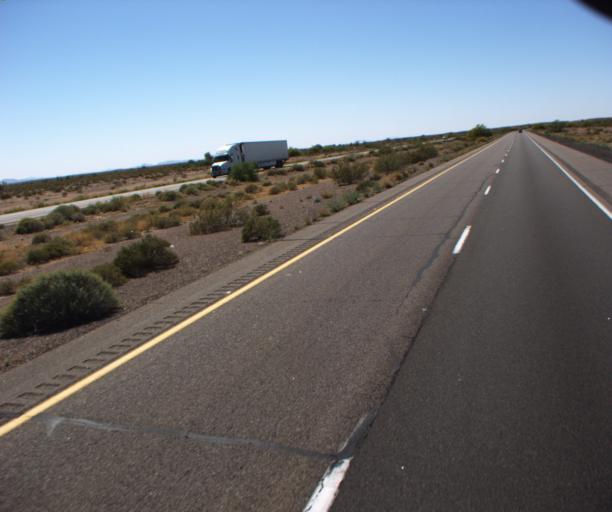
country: US
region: Arizona
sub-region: Maricopa County
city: Gila Bend
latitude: 32.8951
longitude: -113.0330
